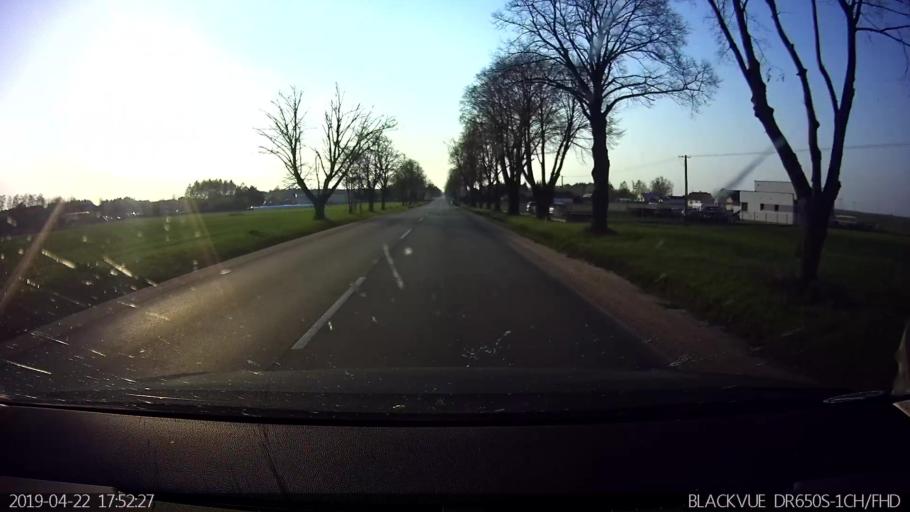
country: PL
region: Masovian Voivodeship
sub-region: Powiat wegrowski
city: Wegrow
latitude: 52.4432
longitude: 21.9758
